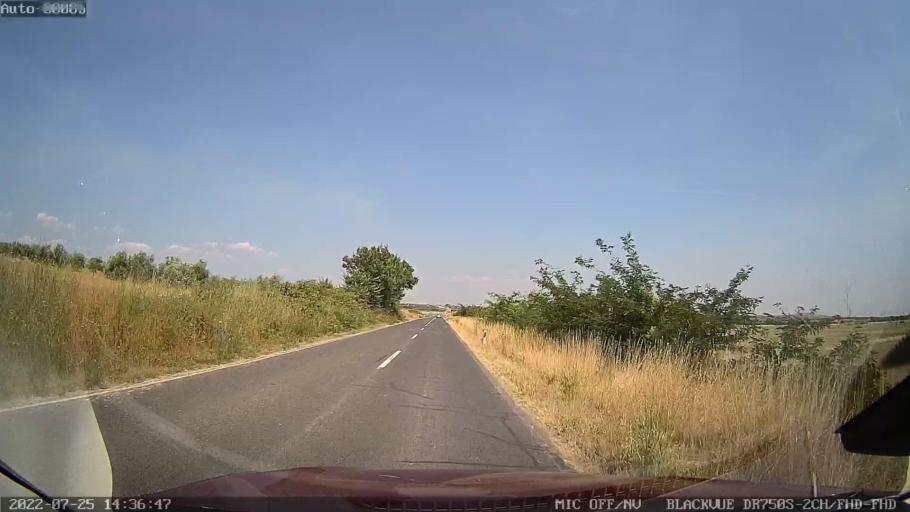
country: HR
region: Zadarska
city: Galovac
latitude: 44.1118
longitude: 15.3898
